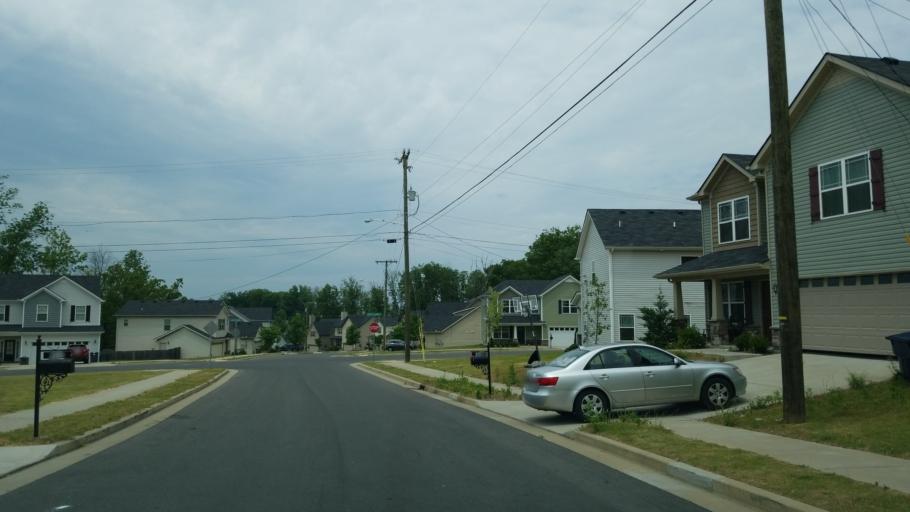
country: US
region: Tennessee
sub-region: Rutherford County
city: La Vergne
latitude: 36.0528
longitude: -86.6030
